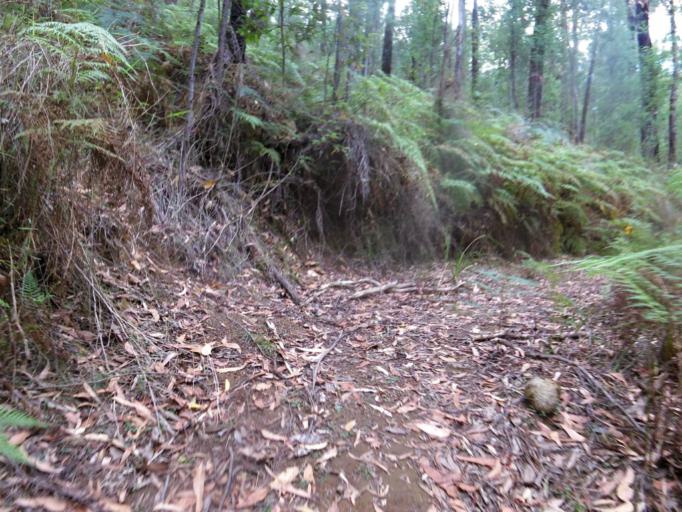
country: AU
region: Victoria
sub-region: Yarra Ranges
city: Healesville
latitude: -37.4290
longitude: 145.5769
